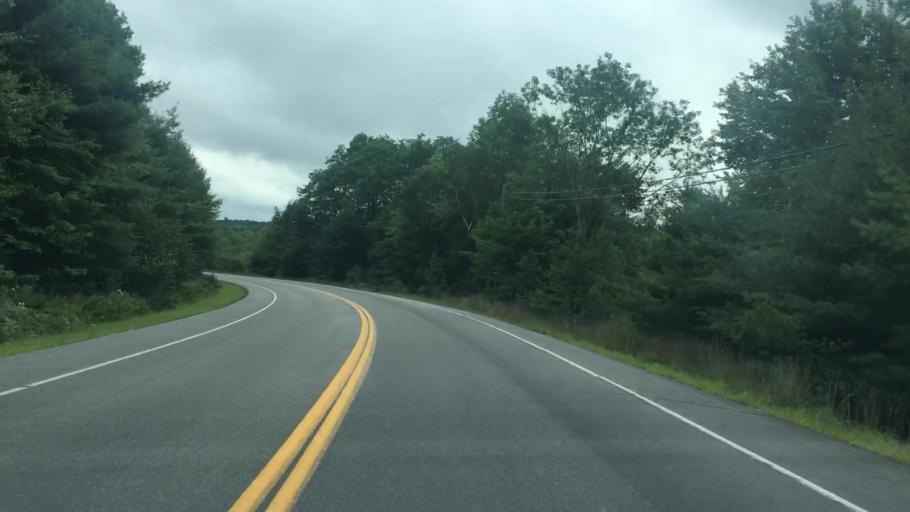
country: US
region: Maine
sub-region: York County
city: Cornish
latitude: 43.7796
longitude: -70.8248
